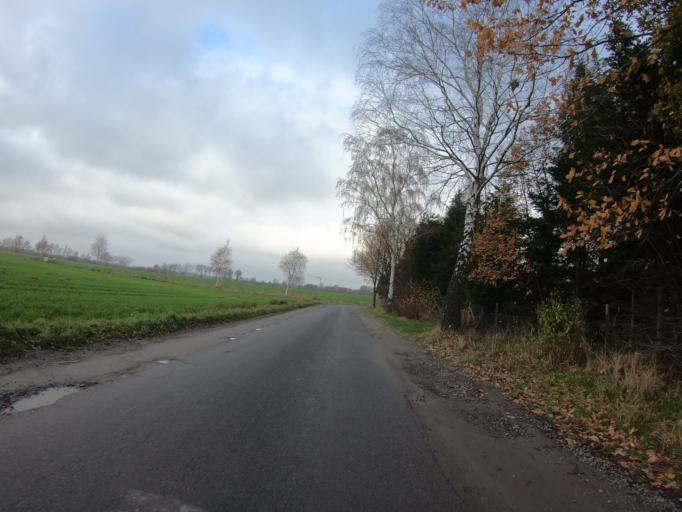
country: DE
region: Lower Saxony
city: Wagenhoff
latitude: 52.5115
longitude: 10.5280
